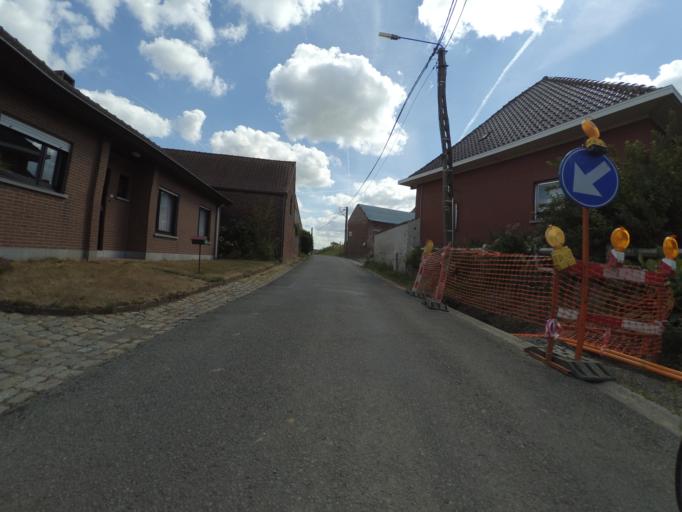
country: BE
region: Wallonia
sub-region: Province du Hainaut
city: Ellezelles
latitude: 50.7265
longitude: 3.6729
